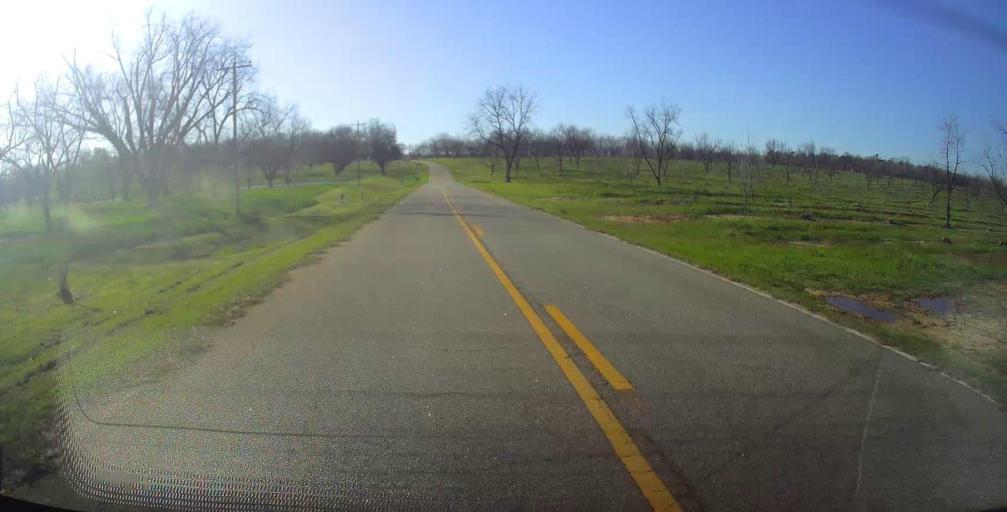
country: US
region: Georgia
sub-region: Houston County
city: Perry
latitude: 32.3660
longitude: -83.6789
